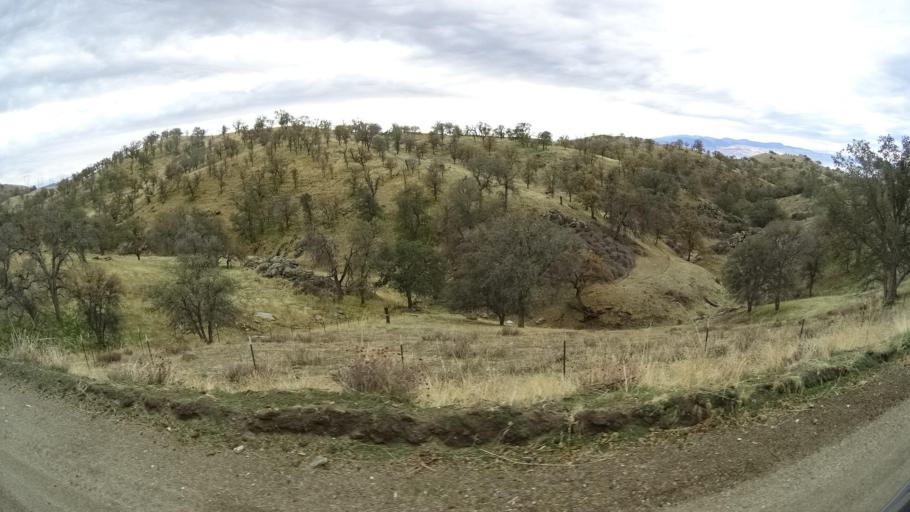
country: US
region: California
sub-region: Kern County
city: Stallion Springs
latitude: 35.1234
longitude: -118.7353
